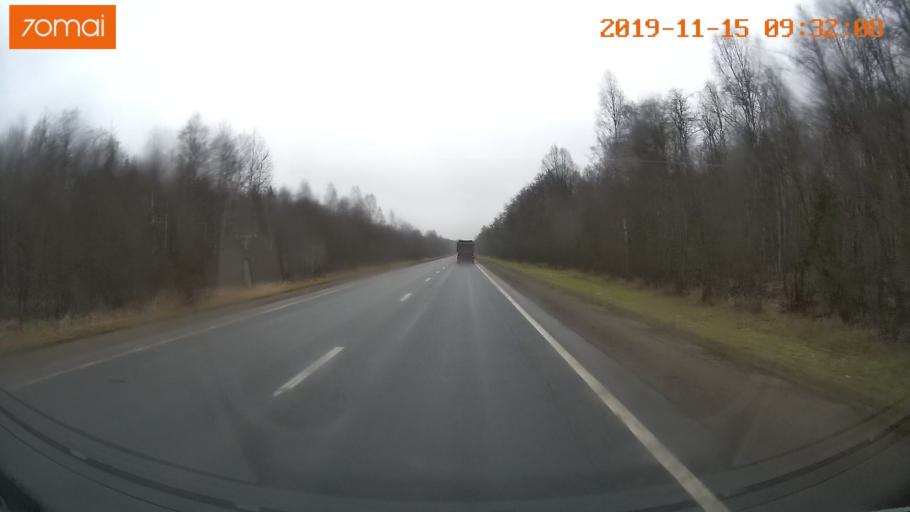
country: RU
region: Vologda
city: Sheksna
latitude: 59.2728
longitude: 38.3279
